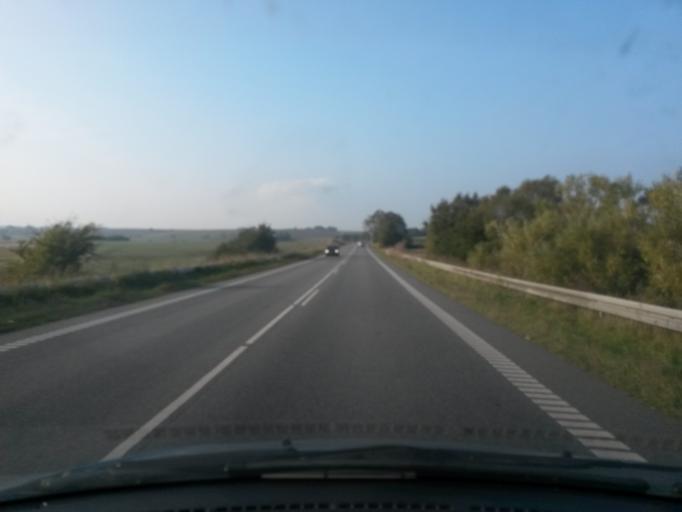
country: DK
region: Central Jutland
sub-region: Syddjurs Kommune
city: Hornslet
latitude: 56.3668
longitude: 10.3229
